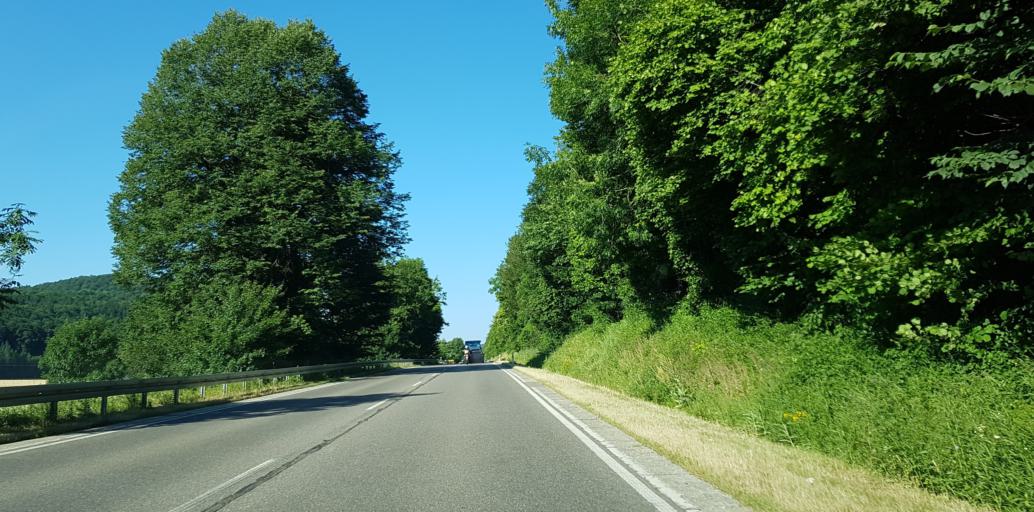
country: DE
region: Baden-Wuerttemberg
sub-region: Tuebingen Region
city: Blaubeuren
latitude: 48.3877
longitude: 9.7634
